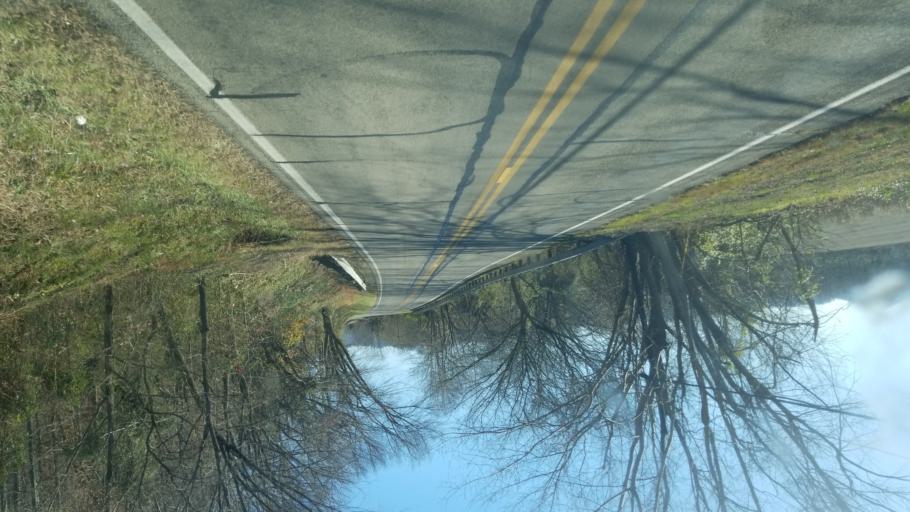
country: US
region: Kentucky
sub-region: Lewis County
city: Vanceburg
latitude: 38.6261
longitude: -83.1633
